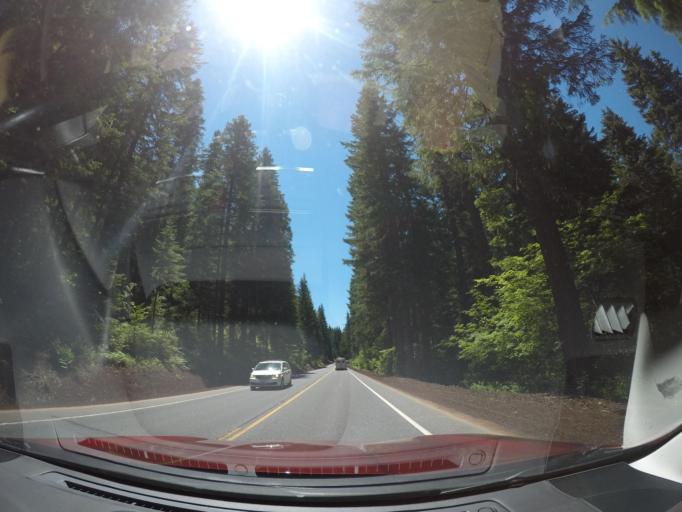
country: US
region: Oregon
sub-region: Deschutes County
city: Sisters
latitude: 44.5272
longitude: -121.9944
